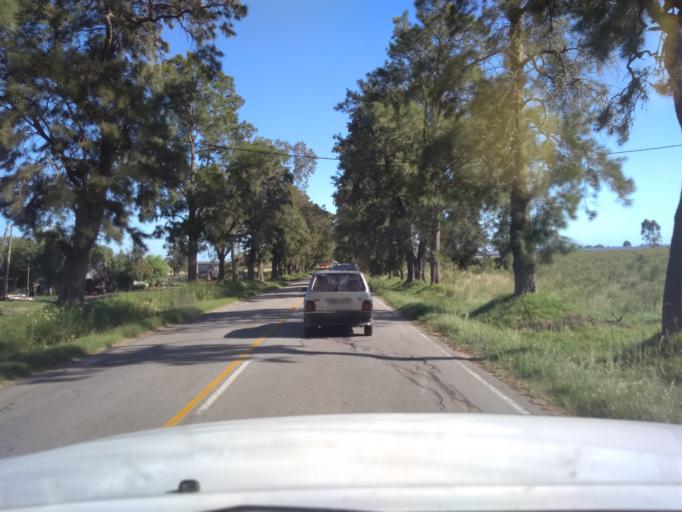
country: UY
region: Canelones
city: San Bautista
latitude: -34.3943
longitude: -55.9596
